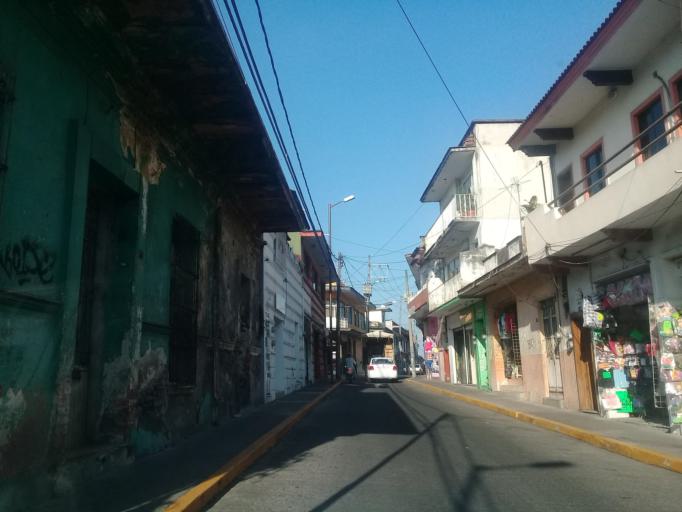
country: MX
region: Veracruz
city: Orizaba
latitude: 18.8496
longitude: -97.1075
